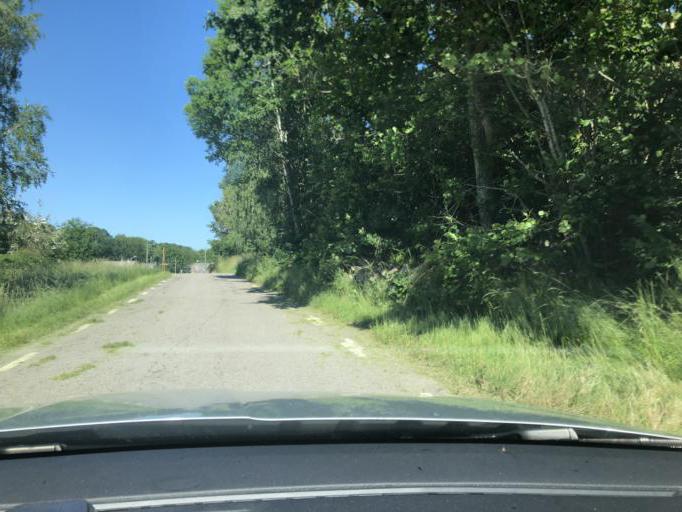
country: SE
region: Blekinge
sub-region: Karlshamns Kommun
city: Morrum
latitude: 56.1882
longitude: 14.6770
